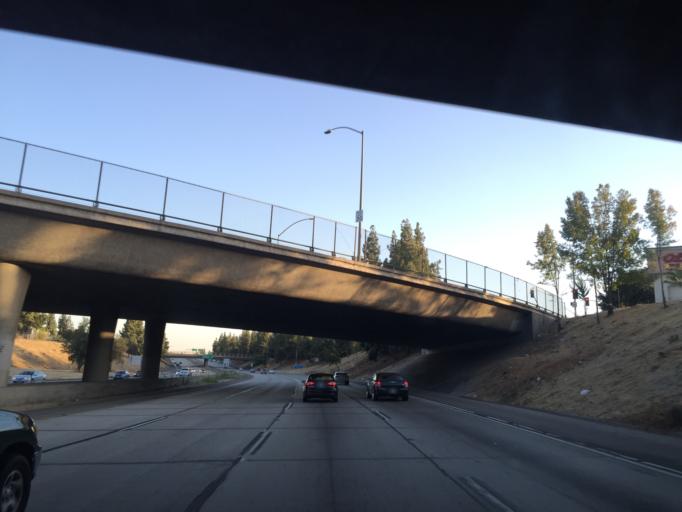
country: US
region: California
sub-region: Fresno County
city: Fresno
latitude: 36.7435
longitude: -119.7774
